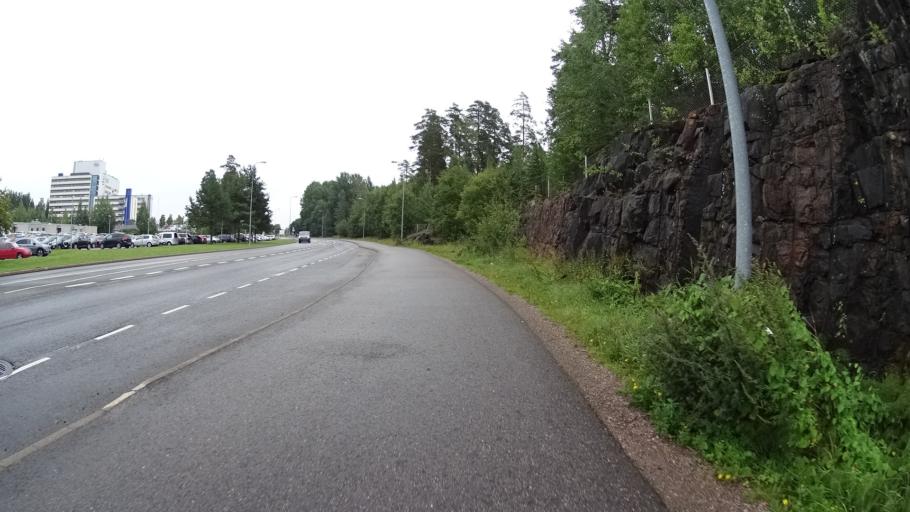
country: FI
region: Uusimaa
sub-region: Helsinki
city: Kauniainen
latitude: 60.2023
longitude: 24.7525
